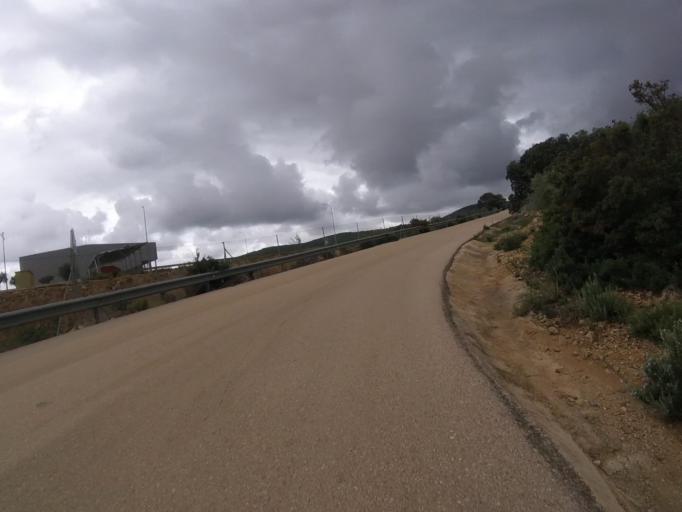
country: ES
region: Valencia
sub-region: Provincia de Castello
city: Benlloch
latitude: 40.2041
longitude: 0.0638
